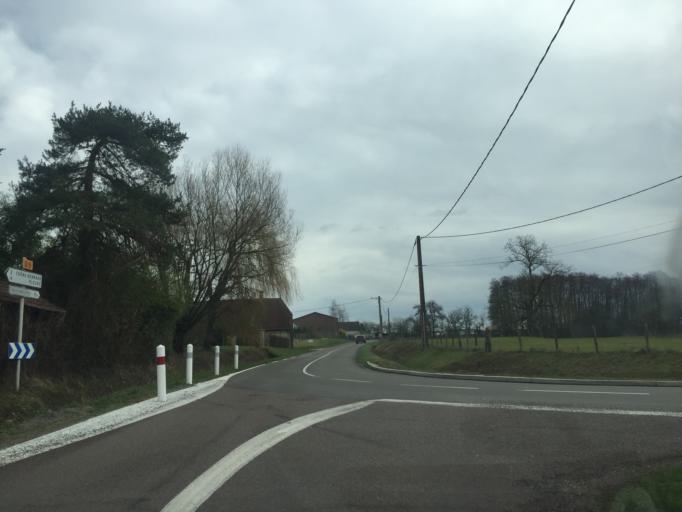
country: FR
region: Franche-Comte
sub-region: Departement du Jura
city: Mont-sous-Vaudrey
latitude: 46.9217
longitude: 5.5095
